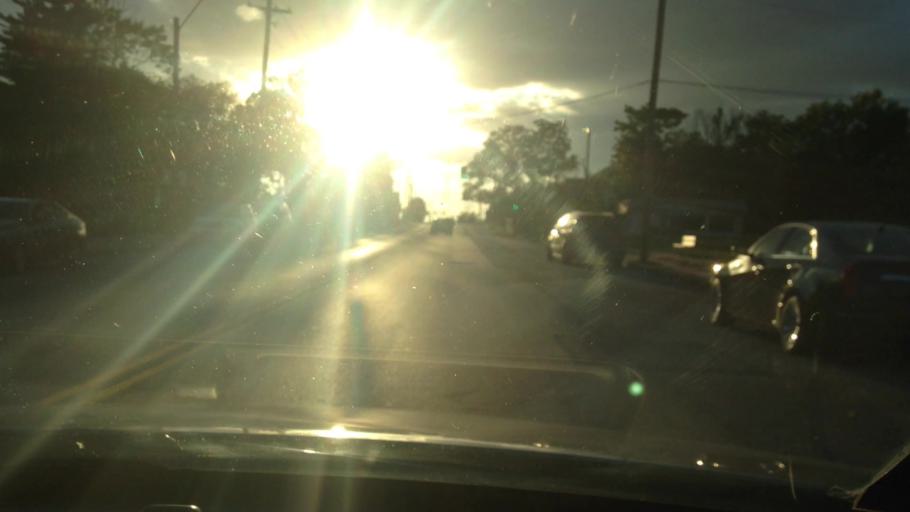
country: US
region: Missouri
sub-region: Jackson County
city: Kansas City
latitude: 39.0697
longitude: -94.5483
